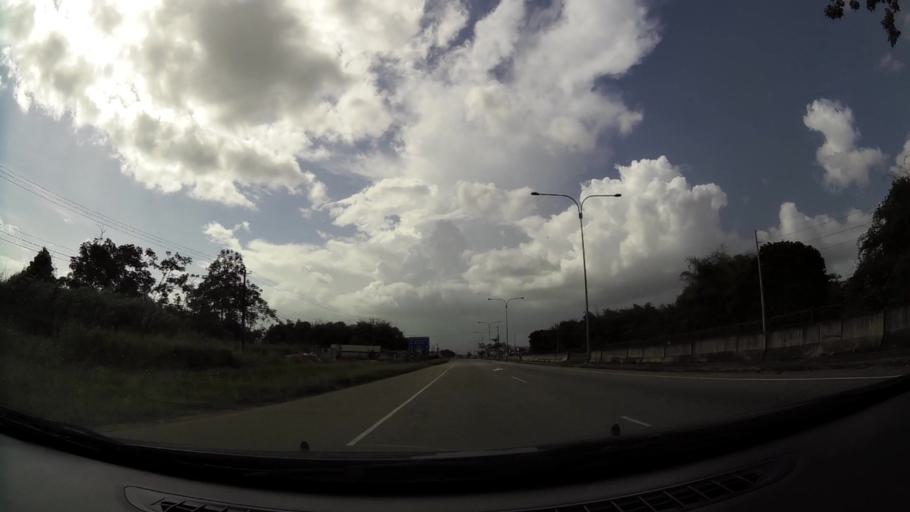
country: TT
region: Tunapuna/Piarco
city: Arouca
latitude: 10.6146
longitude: -61.3398
